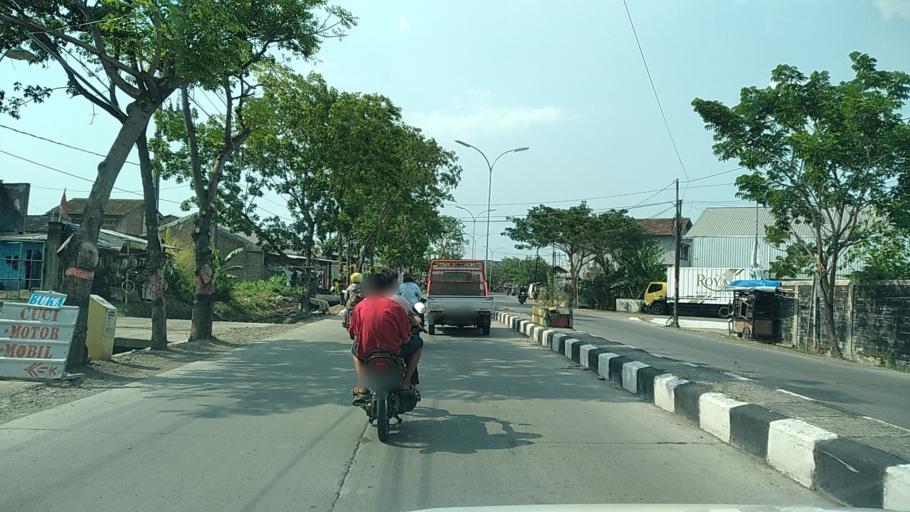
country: ID
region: Central Java
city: Semarang
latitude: -6.9646
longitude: 110.4789
